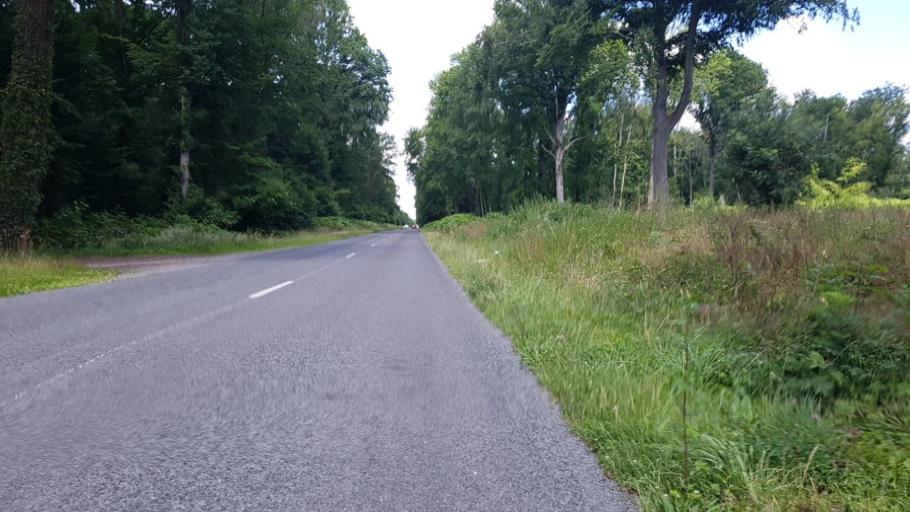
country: FR
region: Picardie
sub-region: Departement de l'Oise
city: Carlepont
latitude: 49.5119
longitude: 2.9833
